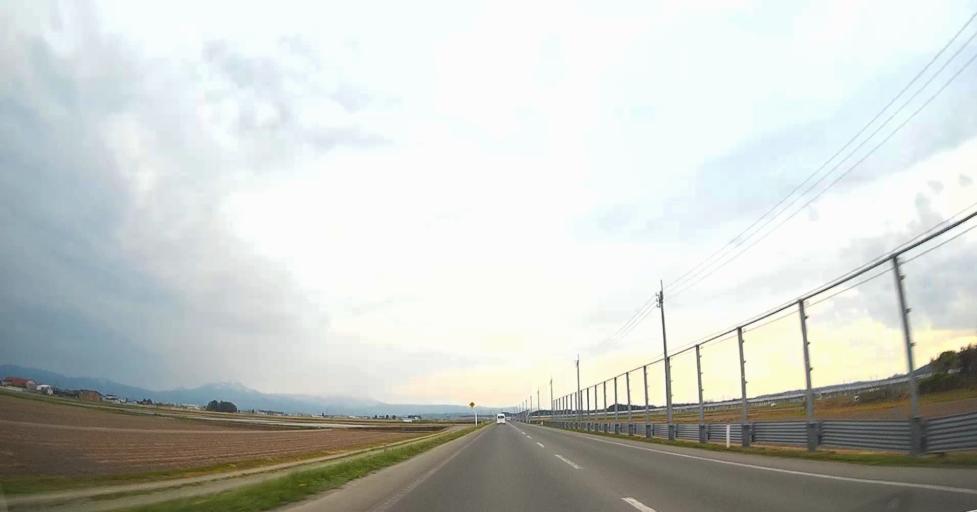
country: JP
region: Aomori
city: Aomori Shi
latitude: 40.8827
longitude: 140.6702
